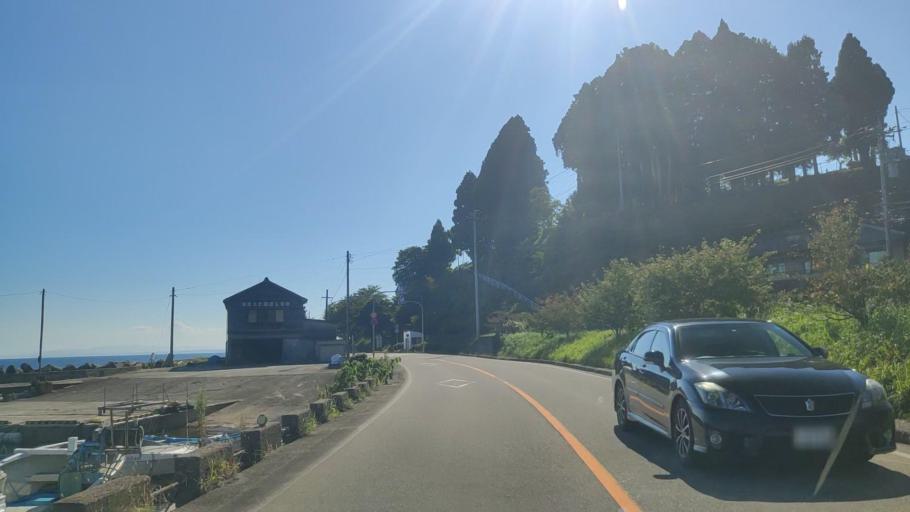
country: JP
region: Ishikawa
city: Nanao
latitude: 37.2884
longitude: 137.1162
